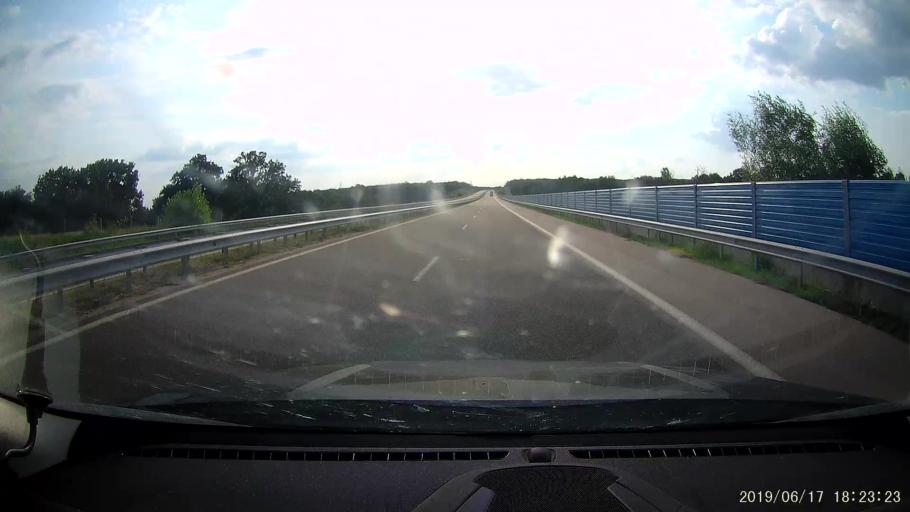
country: BG
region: Khaskovo
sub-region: Obshtina Simeonovgrad
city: Simeonovgrad
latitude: 41.9754
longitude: 25.7231
